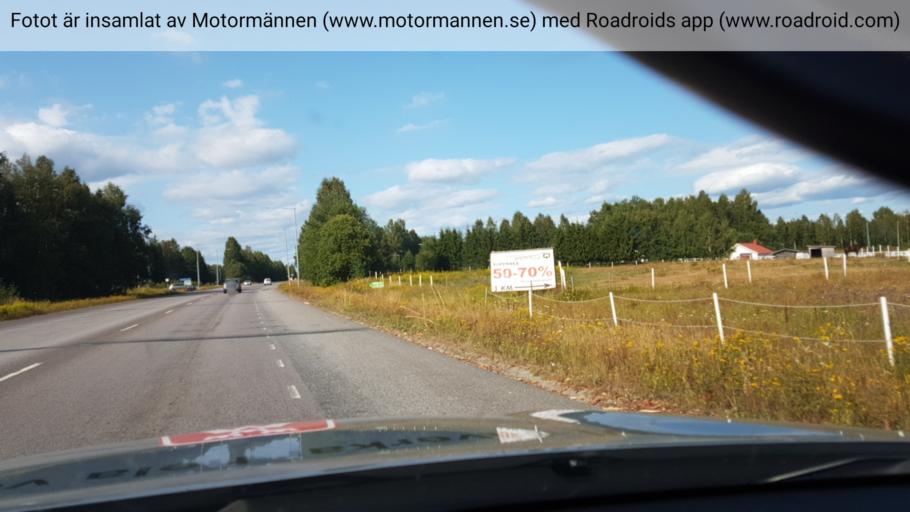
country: SE
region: Norrbotten
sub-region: Pitea Kommun
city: Pitea
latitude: 65.2846
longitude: 21.5080
